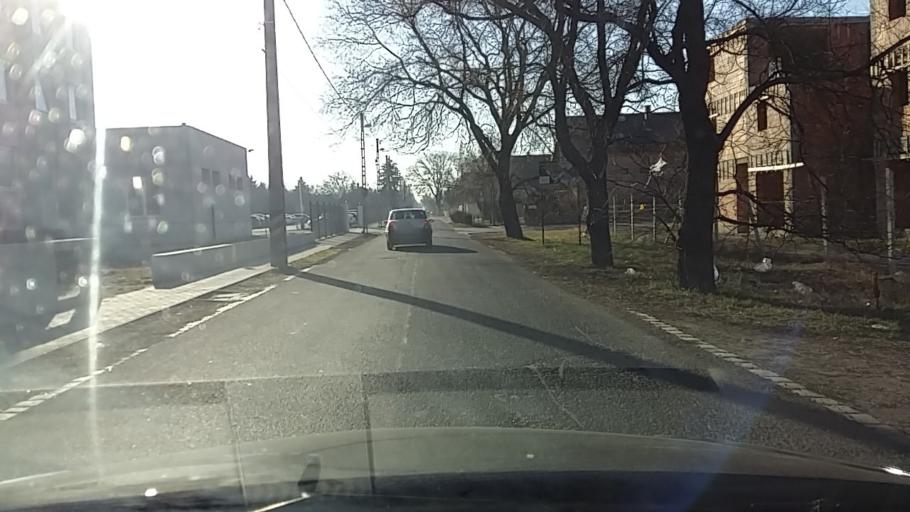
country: HU
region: Budapest
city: Budapest XVI. keruelet
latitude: 47.5334
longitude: 19.1622
